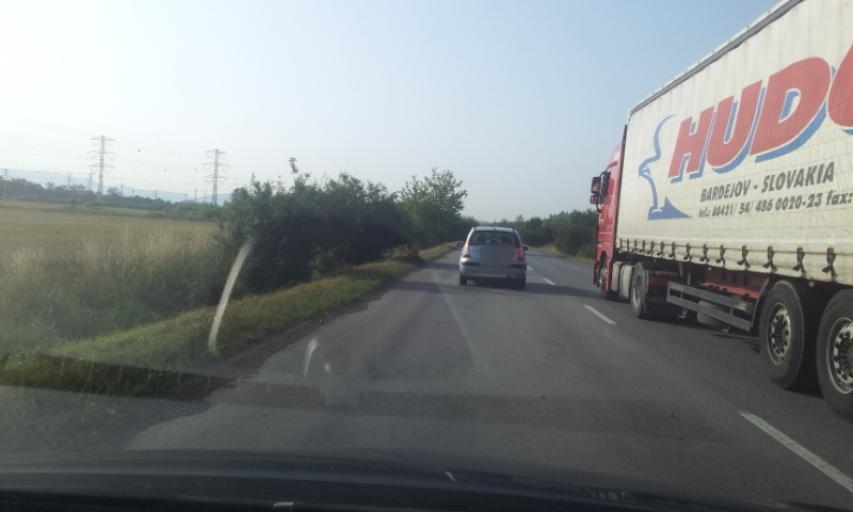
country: SK
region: Kosicky
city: Kosice
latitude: 48.6286
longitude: 21.2195
